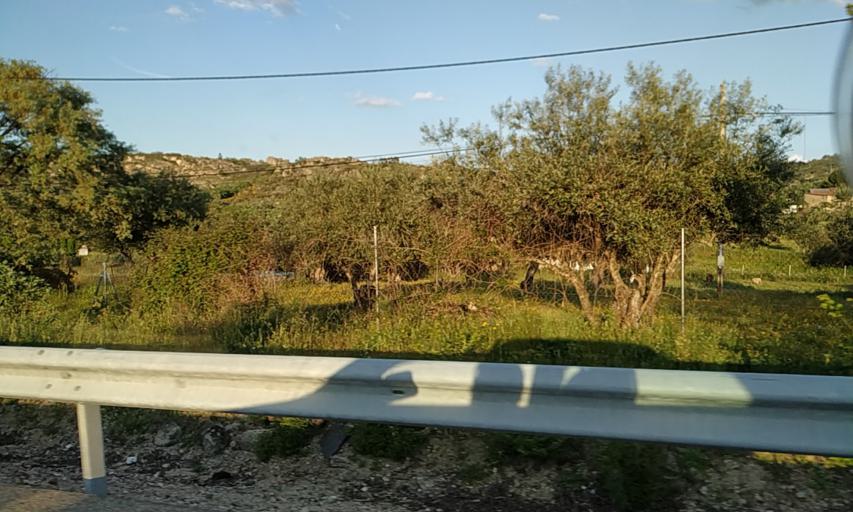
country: PT
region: Portalegre
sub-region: Portalegre
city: Sao Juliao
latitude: 39.3611
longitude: -7.2739
